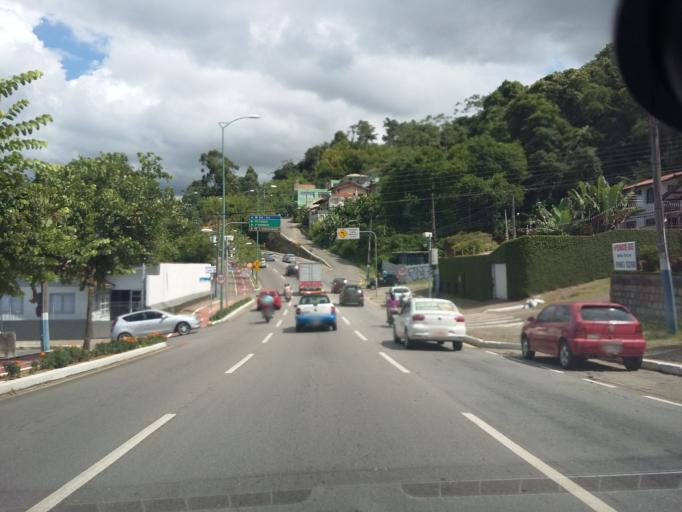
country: BR
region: Santa Catarina
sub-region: Balneario Camboriu
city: Balneario Camboriu
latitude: -26.9874
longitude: -48.6429
